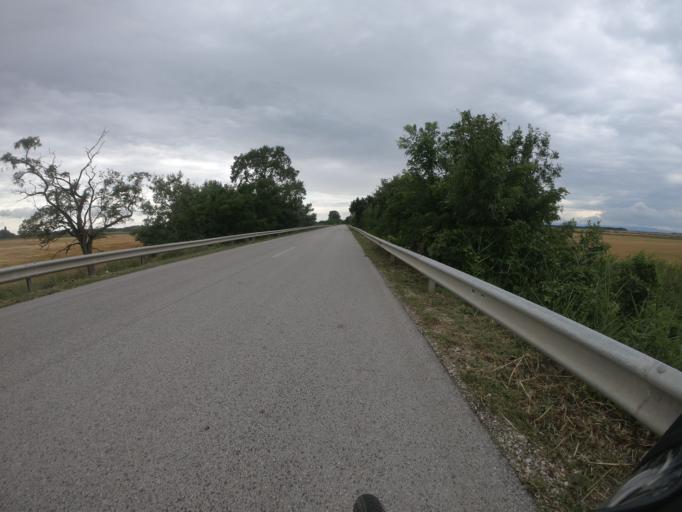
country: HU
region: Heves
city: Poroszlo
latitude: 47.6939
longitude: 20.7331
